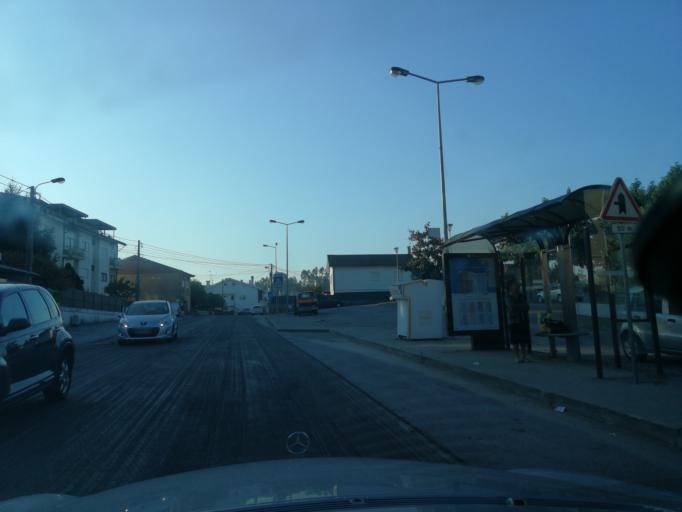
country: PT
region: Braga
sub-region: Braga
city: Braga
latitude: 41.5307
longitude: -8.4272
